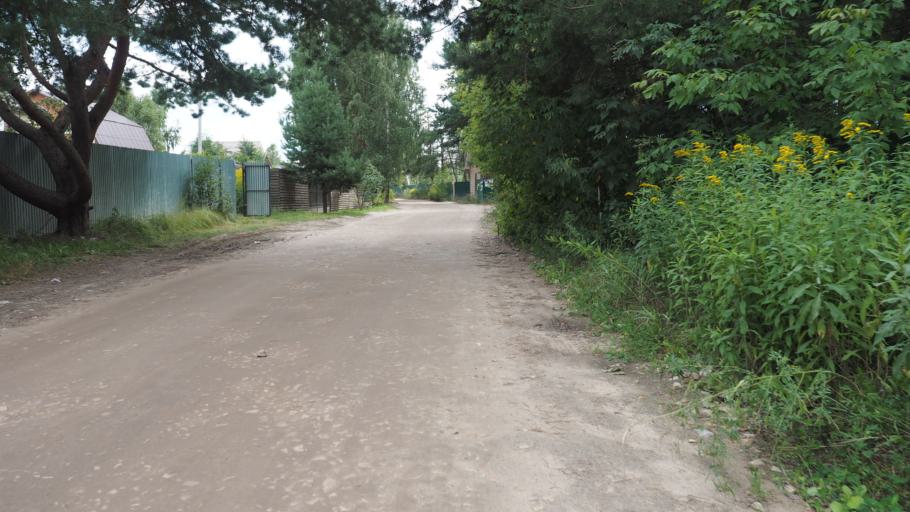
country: RU
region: Moskovskaya
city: Ramenskoye
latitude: 55.5738
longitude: 38.2711
